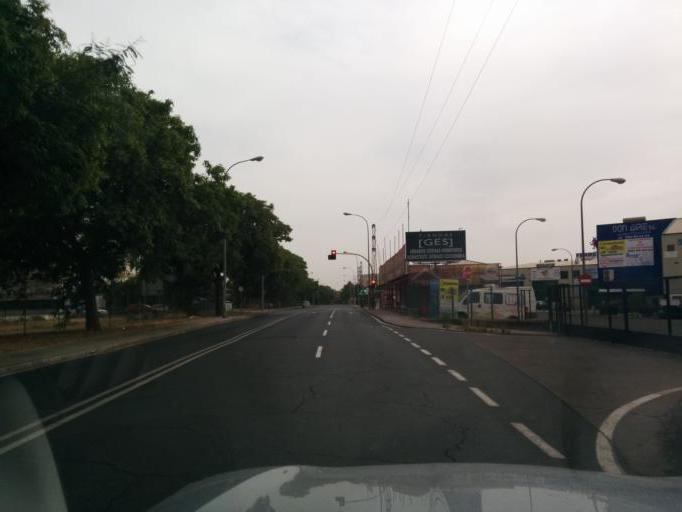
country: ES
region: Andalusia
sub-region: Provincia de Sevilla
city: Sevilla
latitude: 37.4130
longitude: -5.9316
